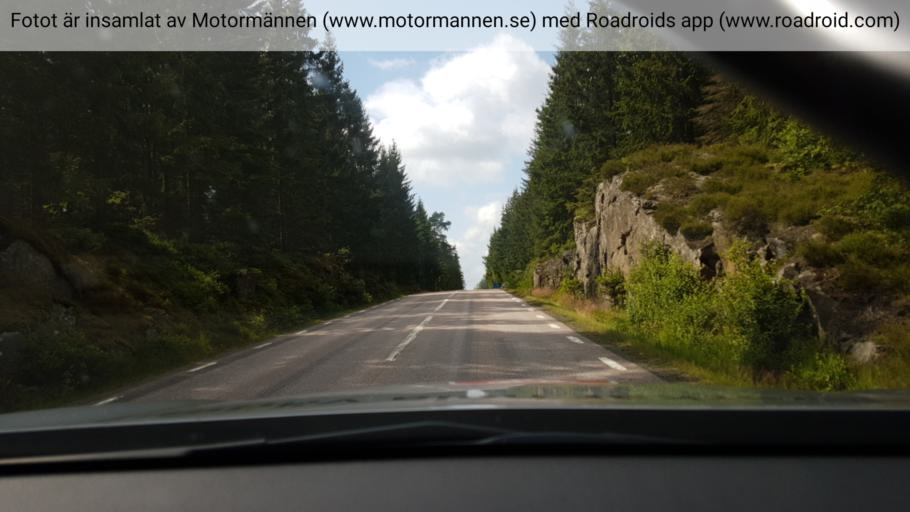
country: SE
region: Vaestra Goetaland
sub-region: Marks Kommun
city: Fritsla
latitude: 57.4902
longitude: 12.8832
